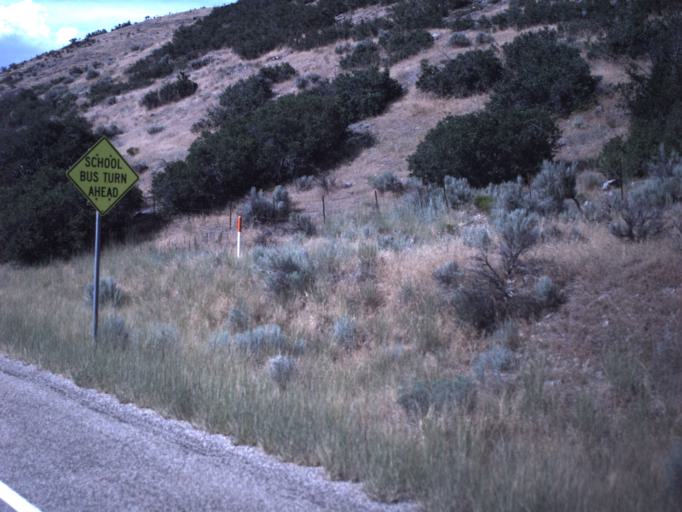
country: US
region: Utah
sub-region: Wasatch County
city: Heber
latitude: 40.4424
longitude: -111.3615
